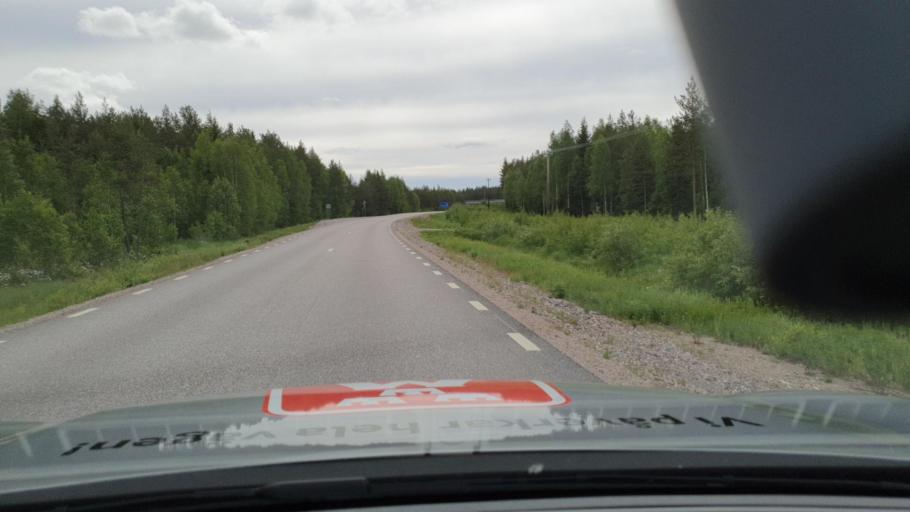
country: SE
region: Norrbotten
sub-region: Kalix Kommun
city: Kalix
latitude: 65.8774
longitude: 23.4844
